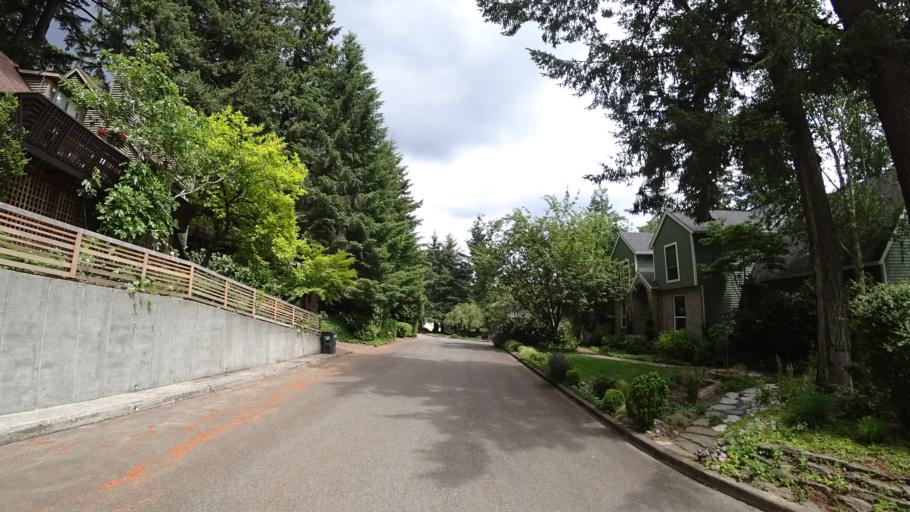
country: US
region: Oregon
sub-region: Clackamas County
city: Lake Oswego
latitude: 45.4473
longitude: -122.7071
